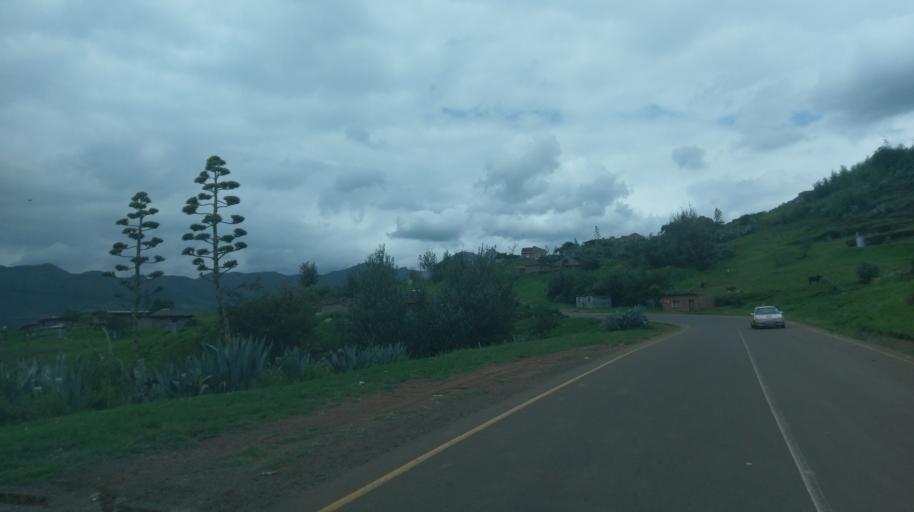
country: LS
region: Butha-Buthe
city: Butha-Buthe
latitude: -29.0337
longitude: 28.2639
